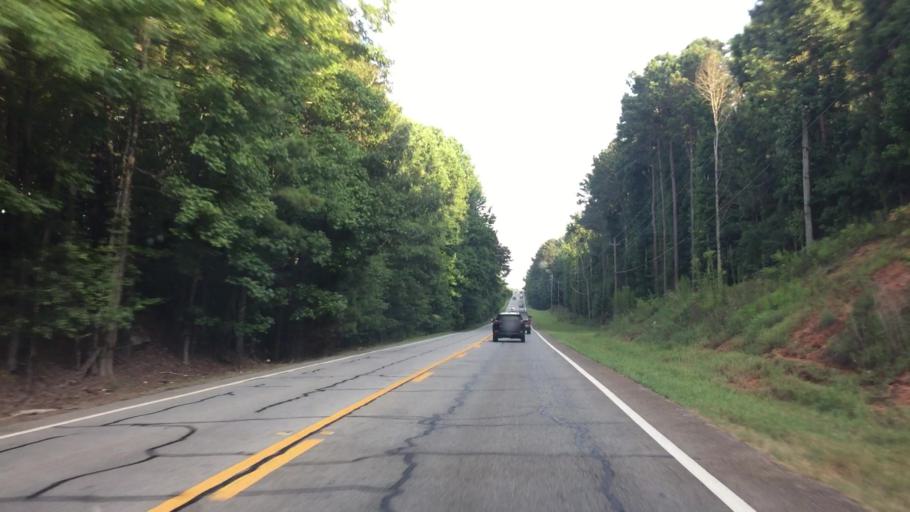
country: US
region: Georgia
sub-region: DeKalb County
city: Pine Mountain
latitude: 33.6204
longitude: -84.1718
